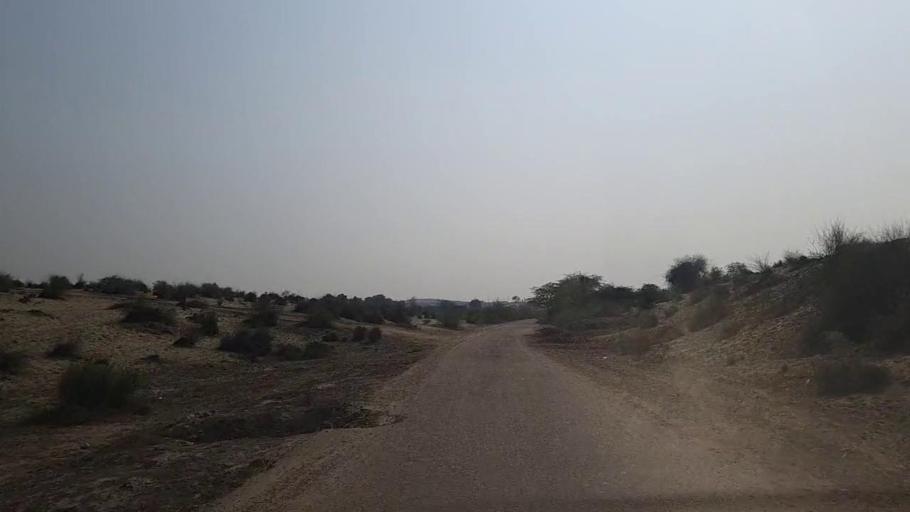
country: PK
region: Sindh
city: Jam Sahib
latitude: 26.4443
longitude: 68.5236
